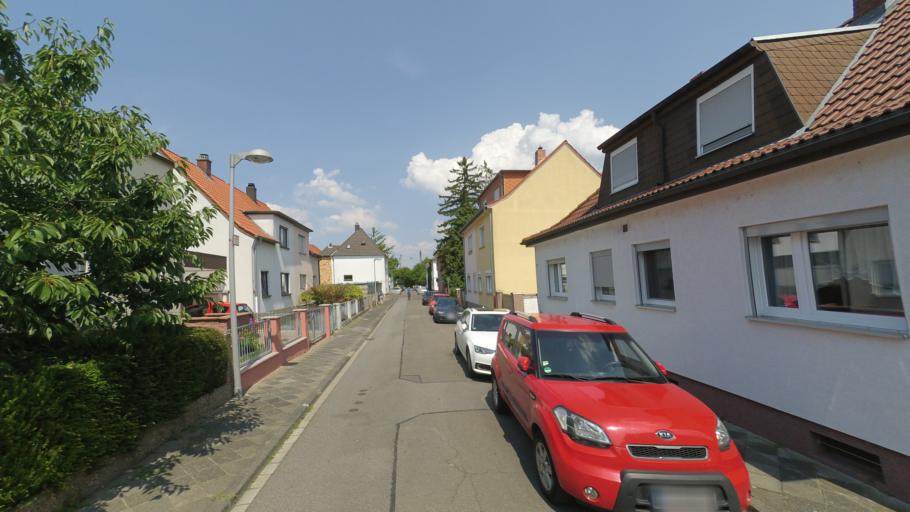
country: DE
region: Rheinland-Pfalz
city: Frankenthal
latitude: 49.5238
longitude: 8.4020
